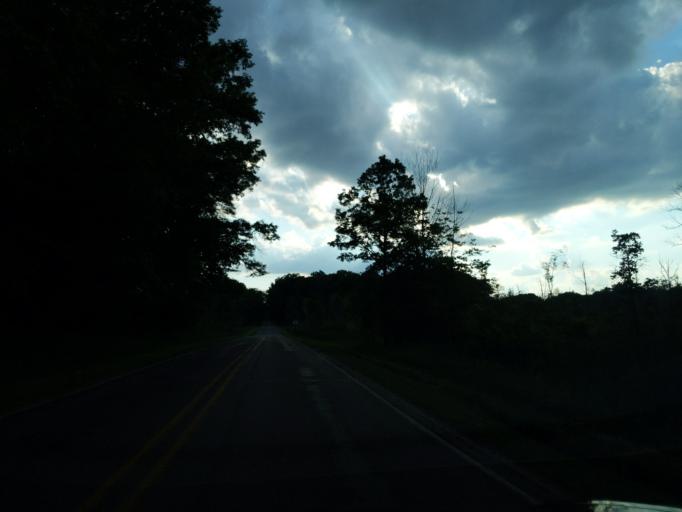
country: US
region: Michigan
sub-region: Ingham County
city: Haslett
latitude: 42.8135
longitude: -84.3759
